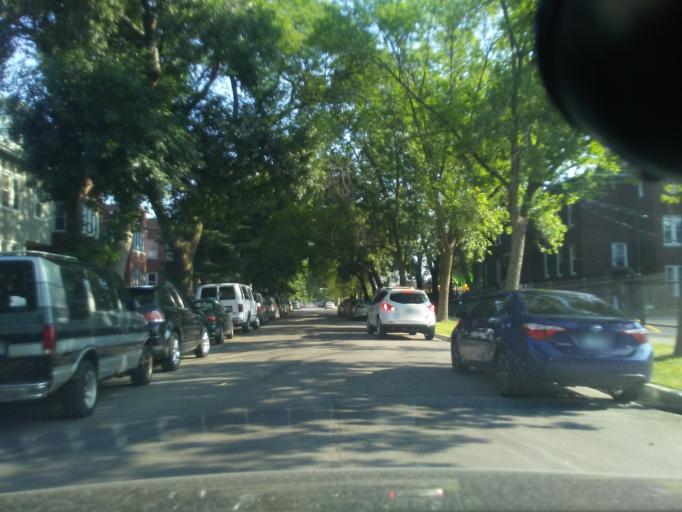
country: US
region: Illinois
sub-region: Cook County
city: Elmwood Park
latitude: 41.9248
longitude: -87.7709
